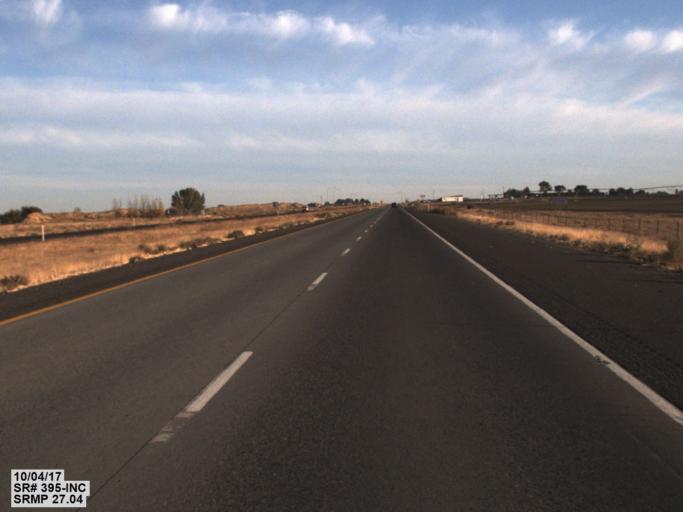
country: US
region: Washington
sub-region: Franklin County
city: Pasco
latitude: 46.3131
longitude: -119.0930
